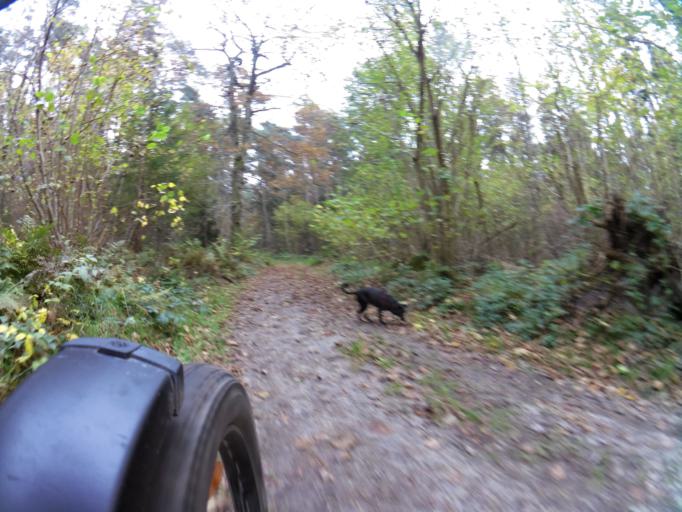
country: PL
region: Pomeranian Voivodeship
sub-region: Powiat pucki
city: Krokowa
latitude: 54.8302
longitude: 18.1167
